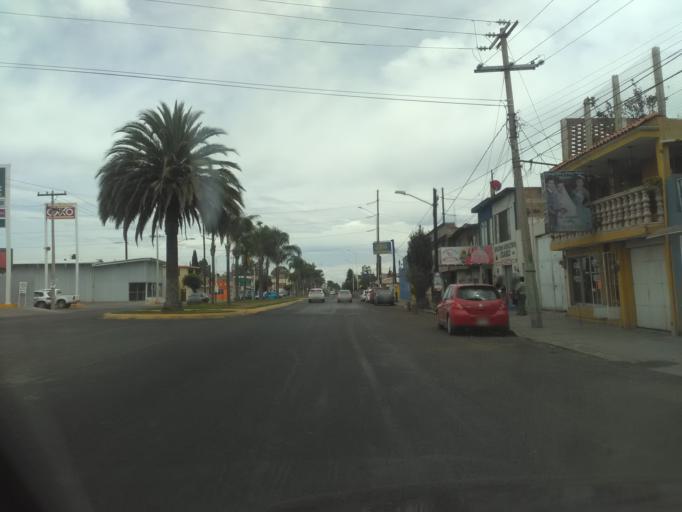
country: MX
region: Durango
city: Victoria de Durango
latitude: 24.0269
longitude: -104.6340
